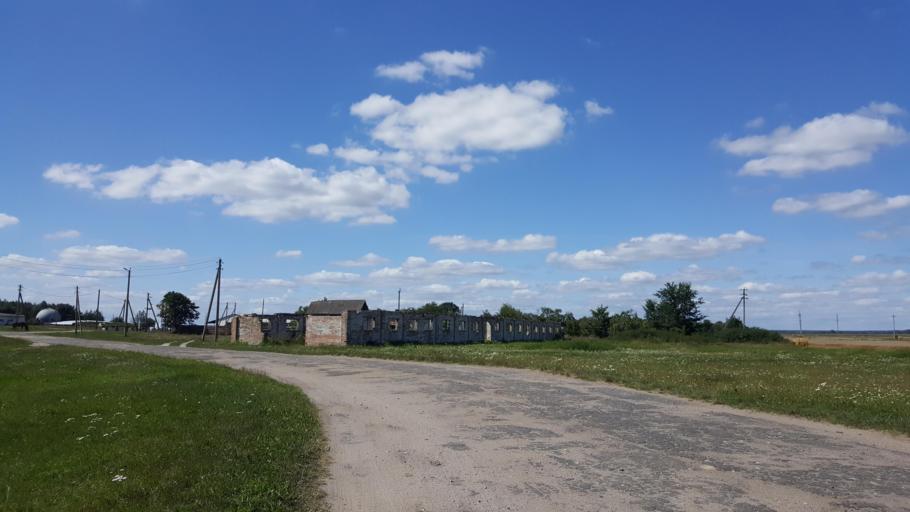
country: BY
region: Brest
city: Kobryn
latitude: 52.2959
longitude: 24.3346
